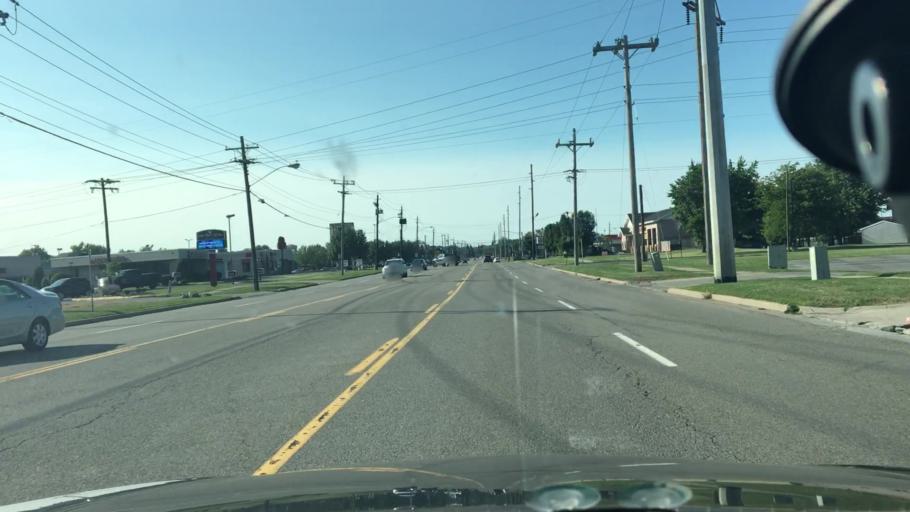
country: US
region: New York
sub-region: Erie County
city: Cheektowaga
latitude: 42.9166
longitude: -78.7358
